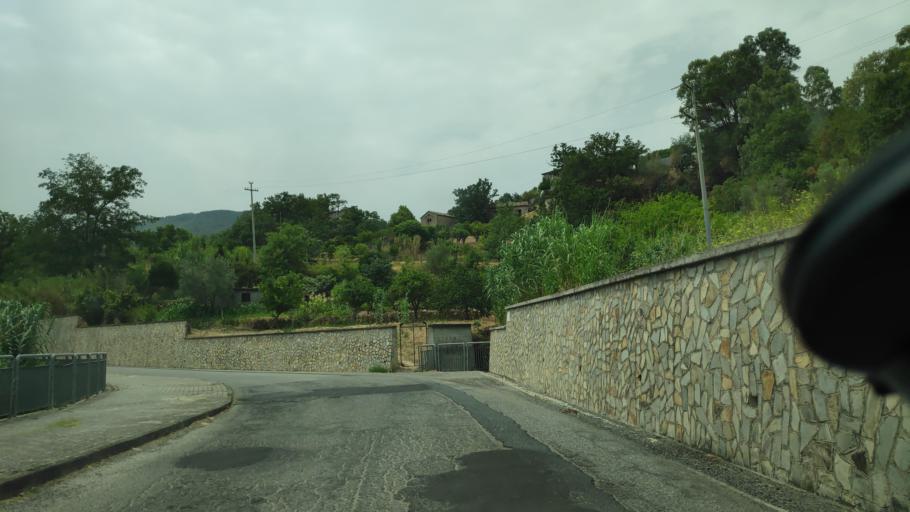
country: IT
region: Calabria
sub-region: Provincia di Catanzaro
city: Davoli
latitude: 38.6549
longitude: 16.4895
